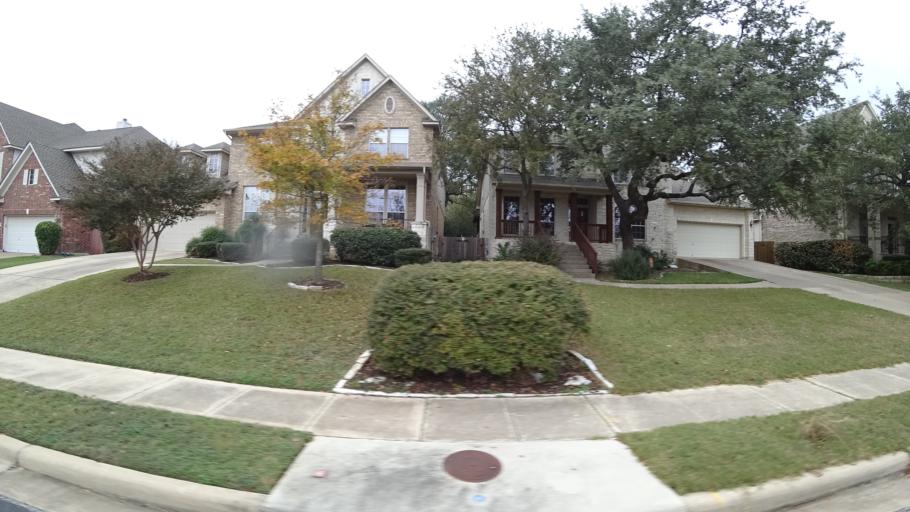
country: US
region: Texas
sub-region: Williamson County
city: Anderson Mill
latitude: 30.4318
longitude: -97.8178
